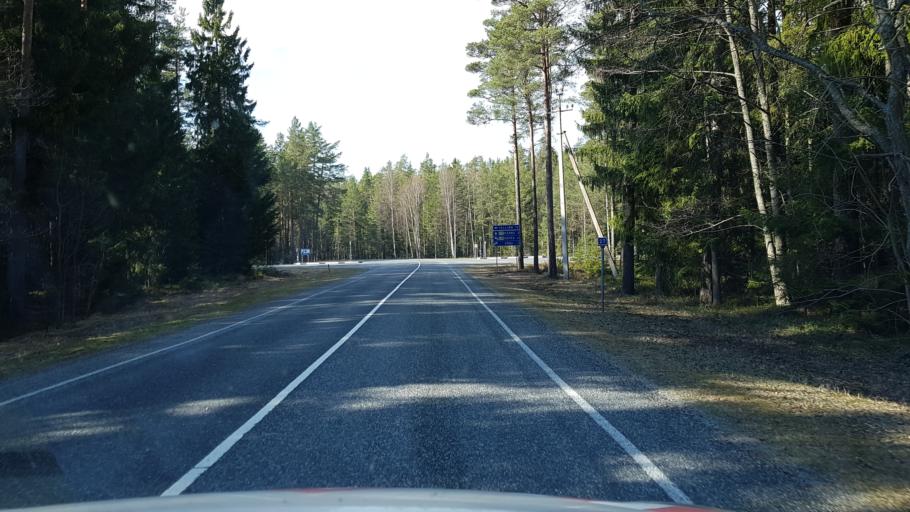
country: EE
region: Harju
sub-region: Loksa linn
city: Loksa
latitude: 59.5749
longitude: 25.9292
